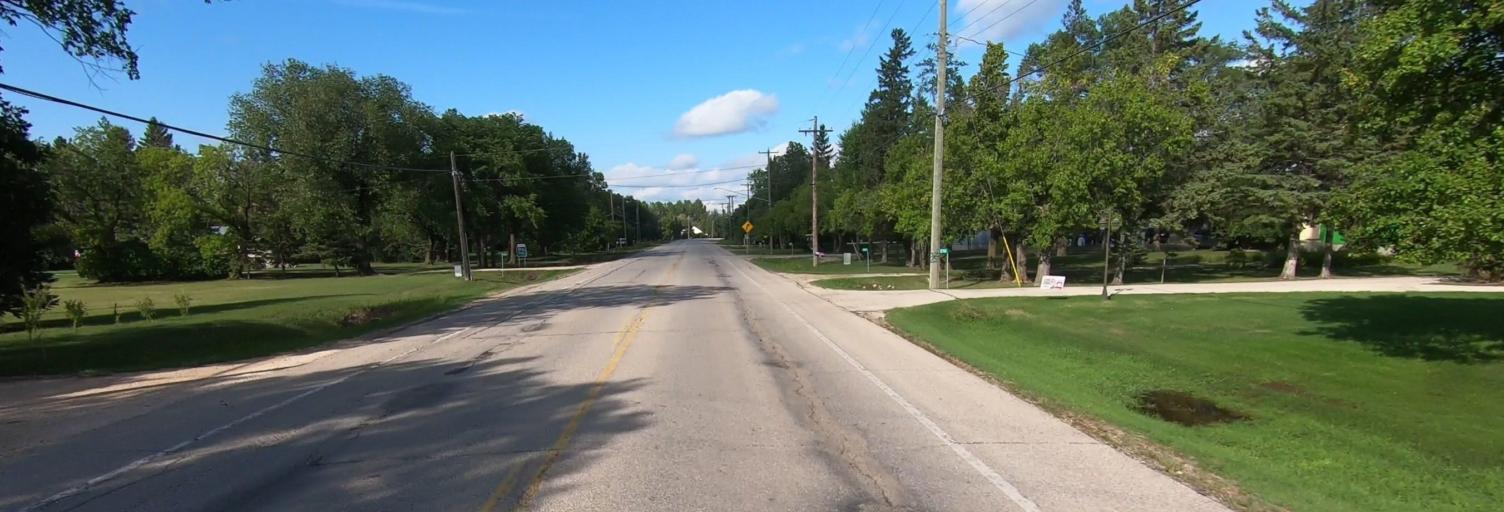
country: CA
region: Manitoba
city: Selkirk
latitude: 50.0573
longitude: -96.9769
